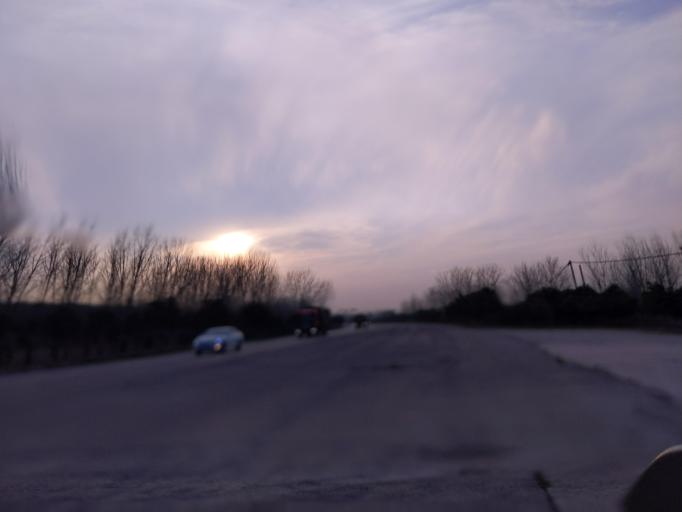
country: CN
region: Henan Sheng
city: Puyang
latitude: 35.8203
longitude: 114.9793
